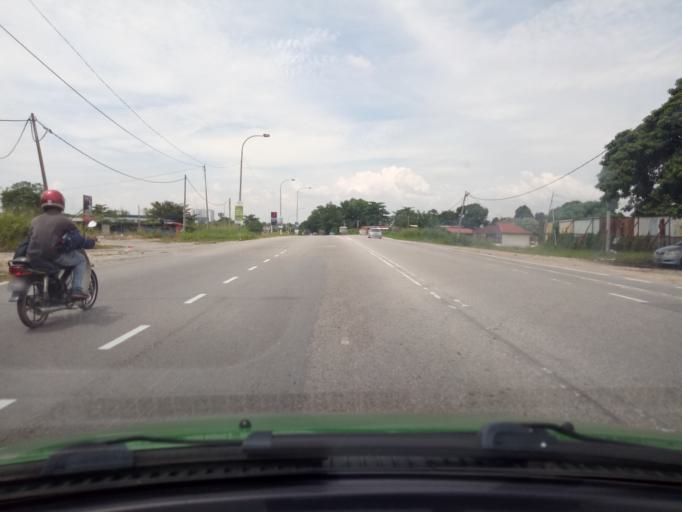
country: MY
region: Selangor
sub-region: Hulu Langat
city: Semenyih
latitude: 2.9395
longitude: 101.8504
